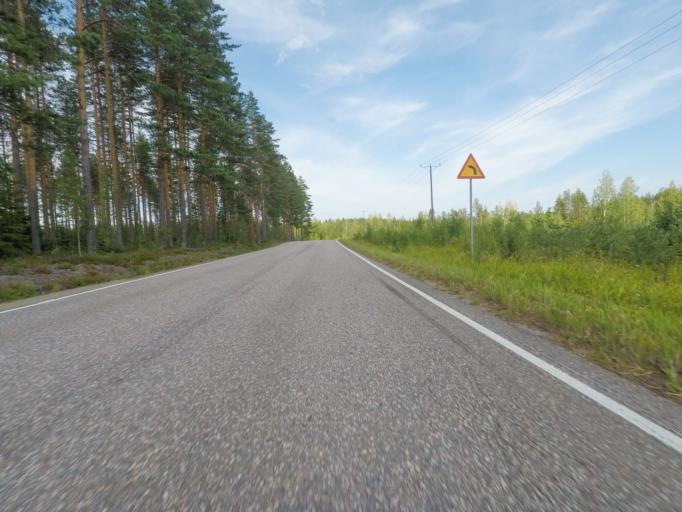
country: FI
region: Southern Savonia
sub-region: Savonlinna
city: Sulkava
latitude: 61.7300
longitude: 28.2080
